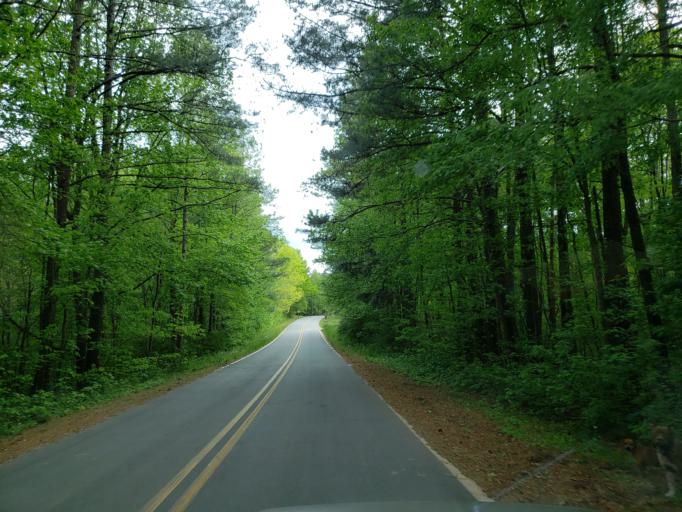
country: US
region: Georgia
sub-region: Haralson County
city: Tallapoosa
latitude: 33.8652
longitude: -85.3624
